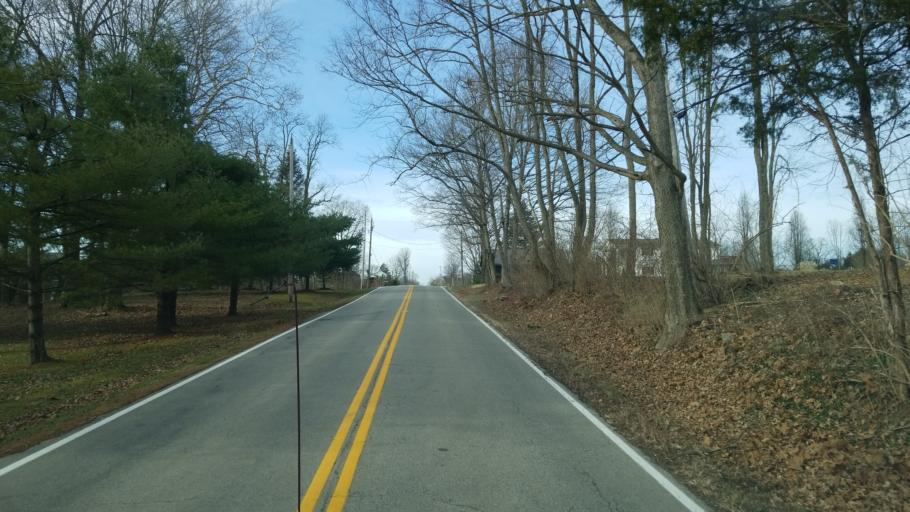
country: US
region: Ohio
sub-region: Warren County
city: Lebanon
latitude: 39.4285
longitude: -84.1364
